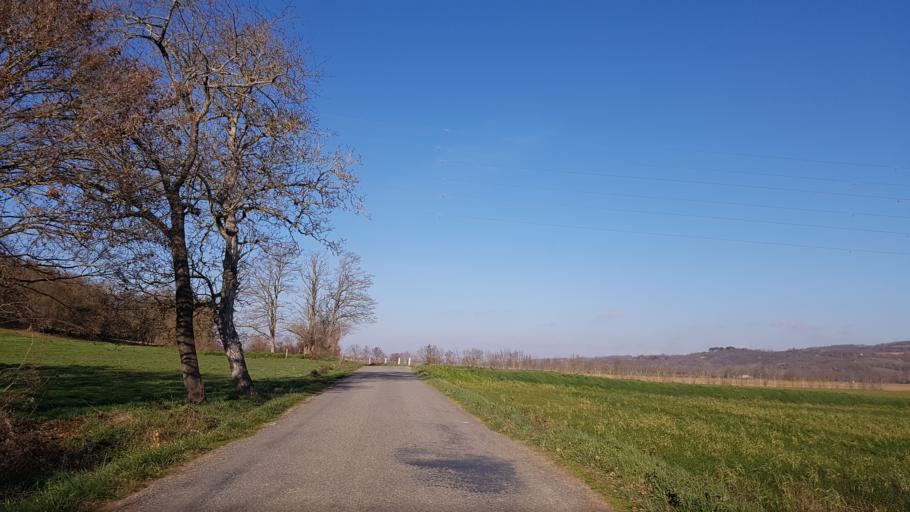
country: FR
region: Midi-Pyrenees
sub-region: Departement de l'Ariege
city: La Tour-du-Crieu
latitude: 43.1233
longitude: 1.7207
